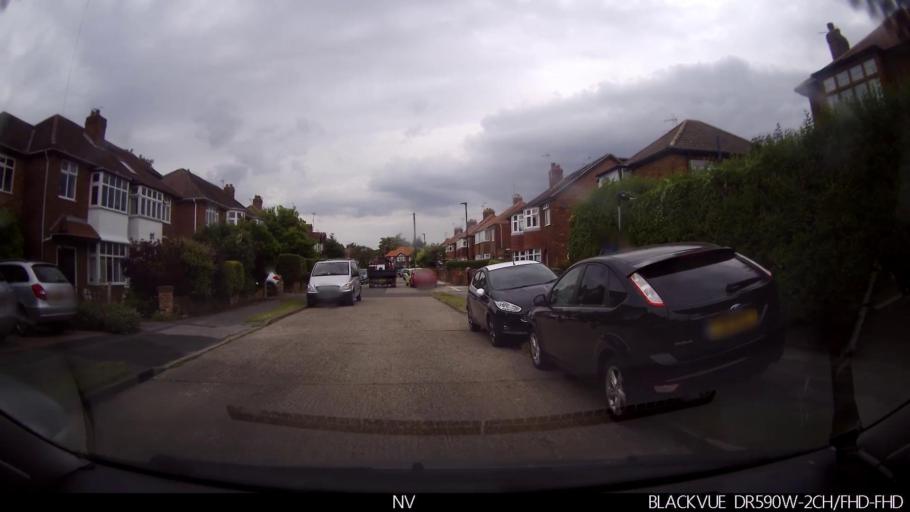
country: GB
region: England
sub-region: City of York
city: Fulford
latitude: 53.9373
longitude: -1.0654
